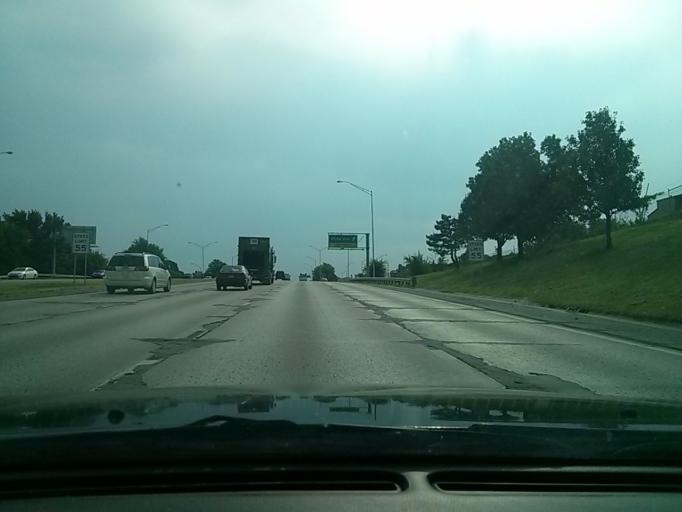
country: US
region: Oklahoma
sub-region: Tulsa County
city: Tulsa
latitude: 36.1427
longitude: -95.9726
